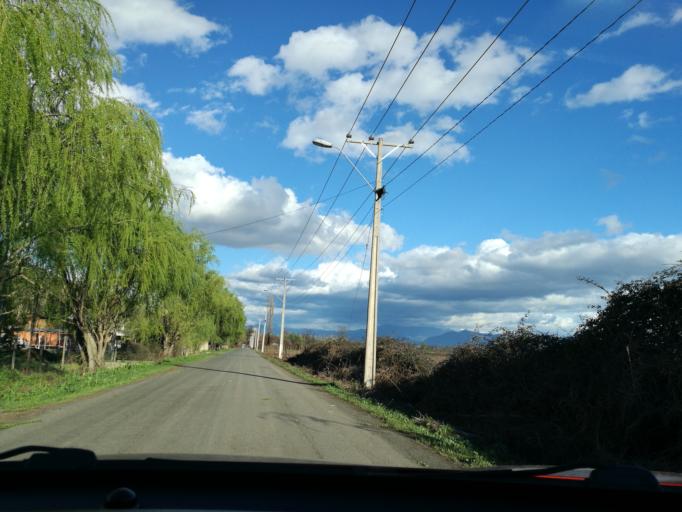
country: CL
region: O'Higgins
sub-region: Provincia de Cachapoal
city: Graneros
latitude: -34.0968
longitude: -70.8166
